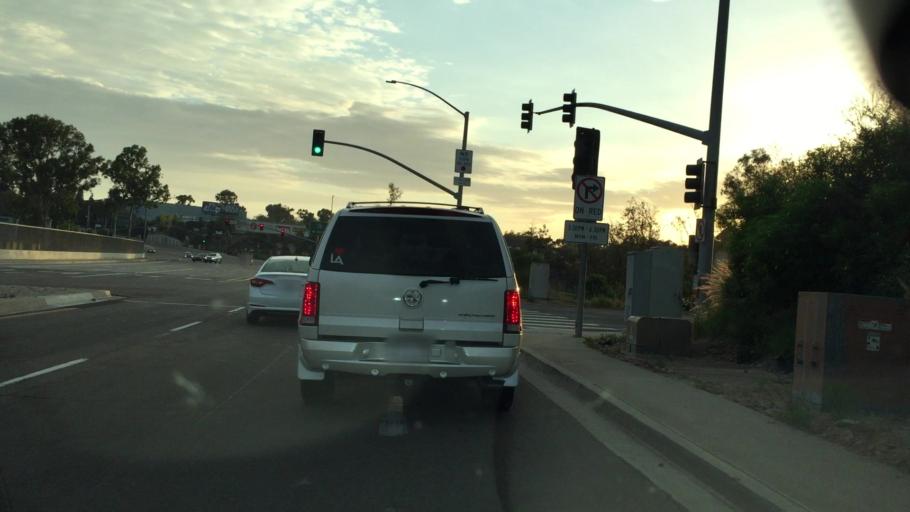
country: US
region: California
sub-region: San Diego County
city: La Mesa
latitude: 32.8339
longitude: -117.1179
